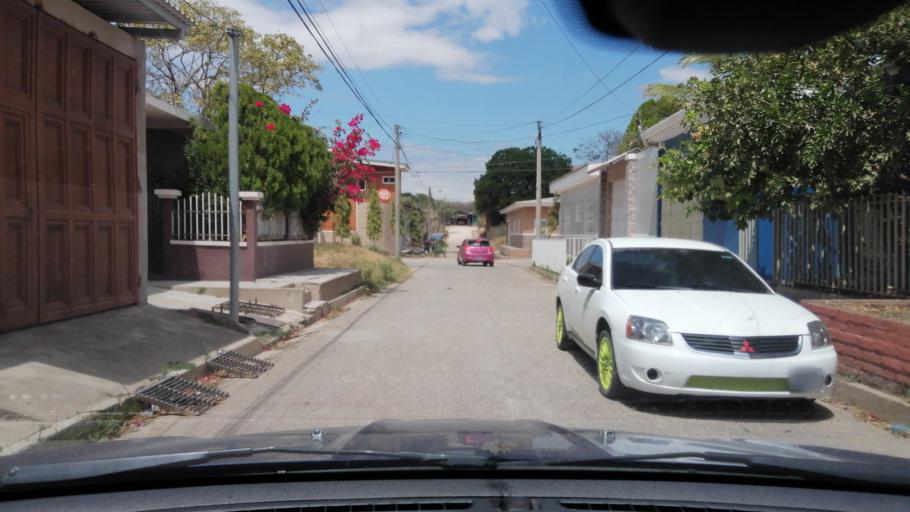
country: SV
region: Santa Ana
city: Metapan
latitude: 14.3353
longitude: -89.4435
